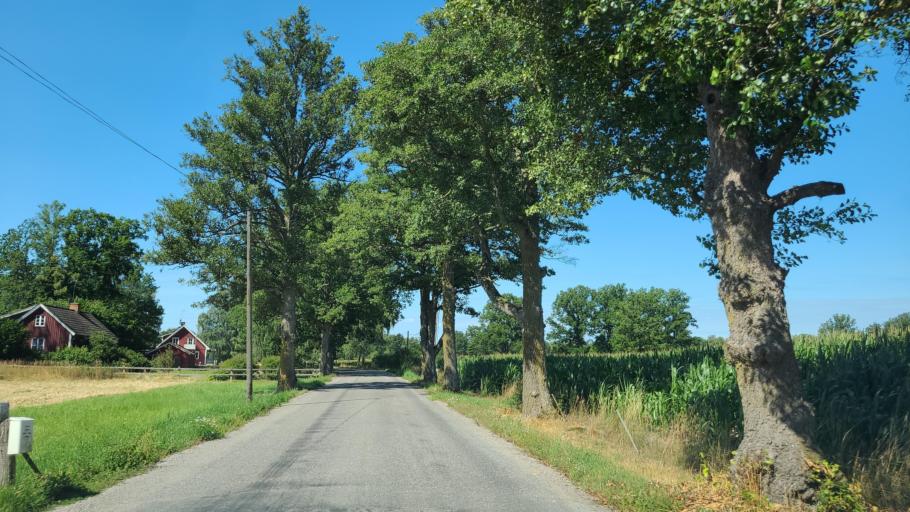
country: SE
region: Kalmar
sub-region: Kalmar Kommun
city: Ljungbyholm
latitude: 56.5760
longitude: 16.0933
